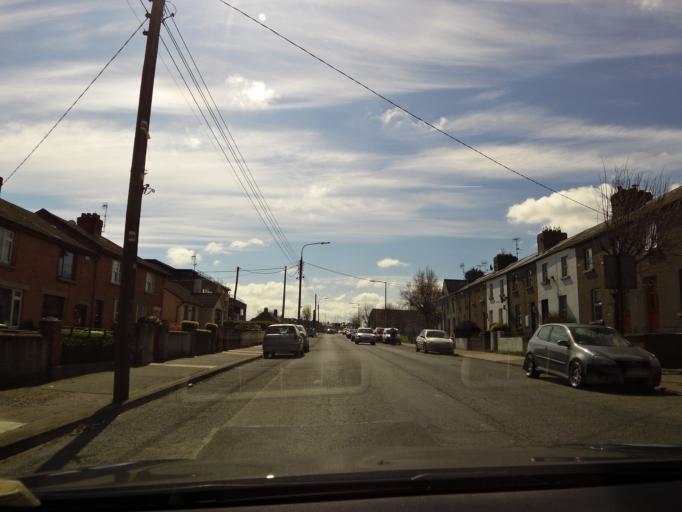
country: IE
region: Leinster
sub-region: Wicklow
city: Arklow
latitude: 52.7924
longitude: -6.1639
